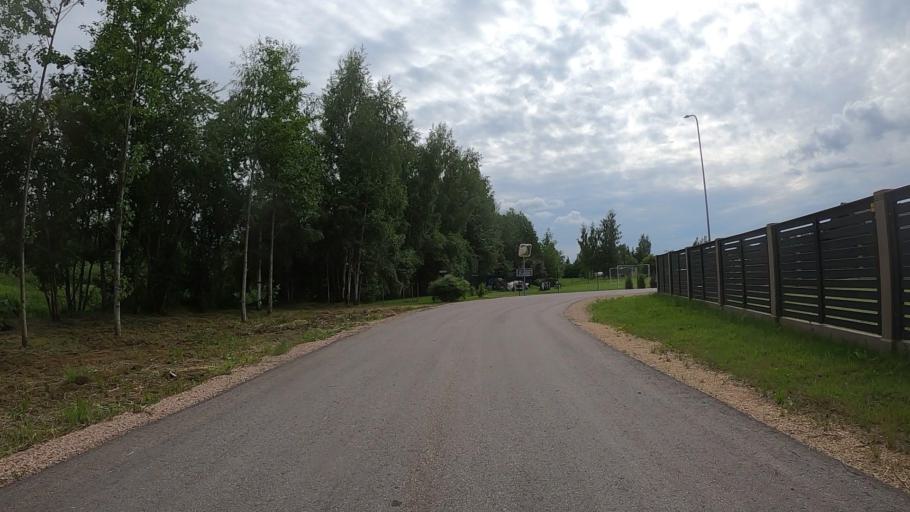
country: LV
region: Olaine
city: Olaine
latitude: 56.7751
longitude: 23.9237
